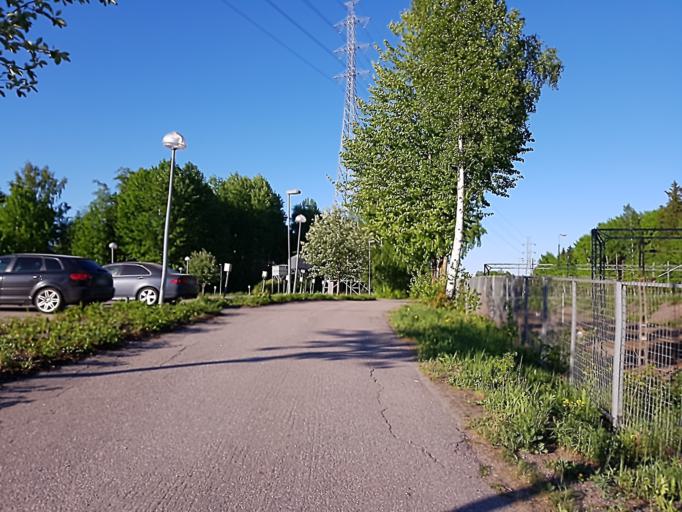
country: FI
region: Uusimaa
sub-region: Helsinki
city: Helsinki
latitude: 60.2219
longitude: 24.9502
